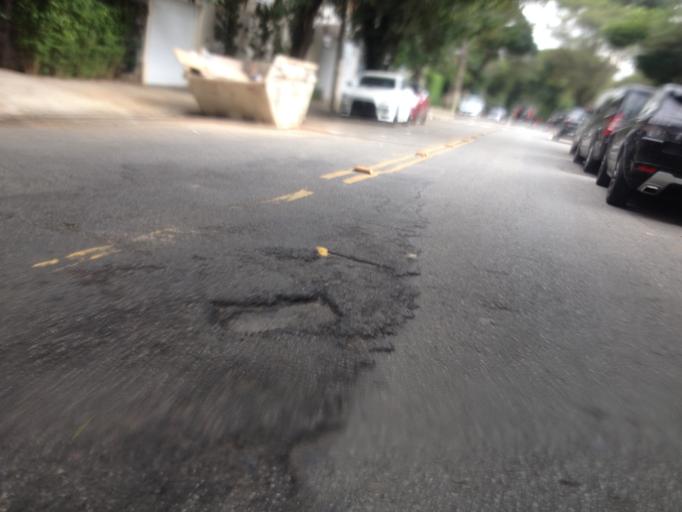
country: BR
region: Sao Paulo
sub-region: Sao Paulo
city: Sao Paulo
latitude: -23.5679
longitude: -46.6826
